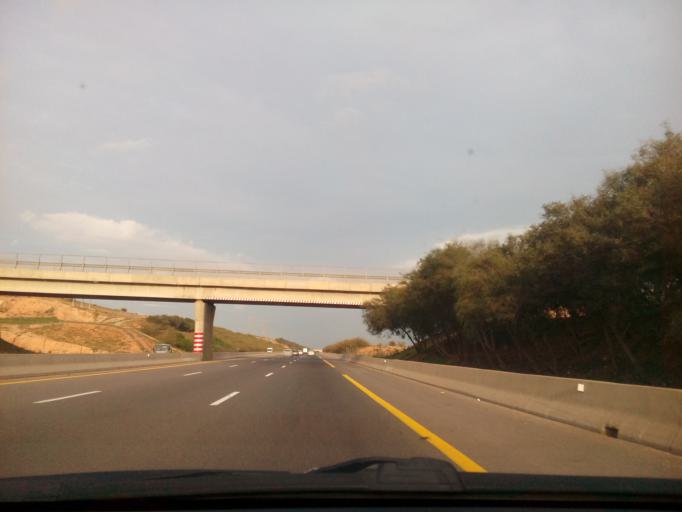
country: DZ
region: Relizane
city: Relizane
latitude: 35.7485
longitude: 0.3495
